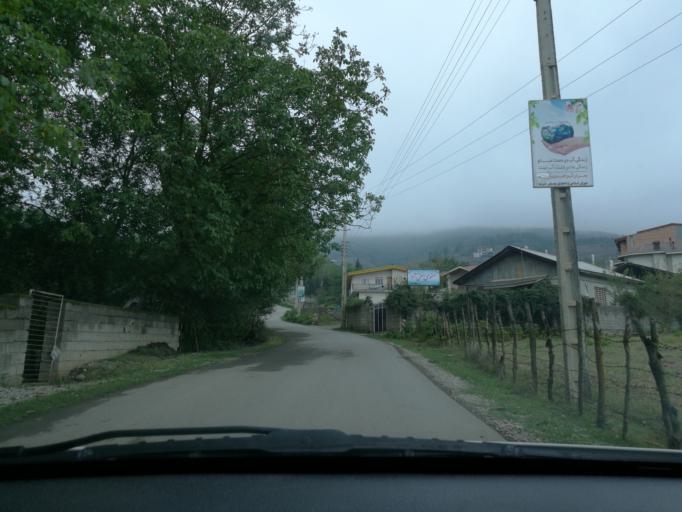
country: IR
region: Mazandaran
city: `Abbasabad
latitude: 36.4988
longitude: 51.2117
